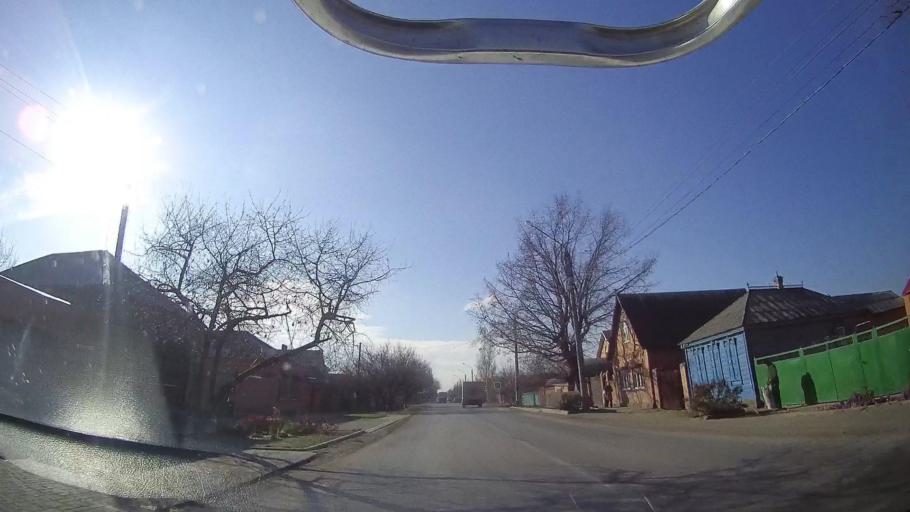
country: RU
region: Rostov
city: Bataysk
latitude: 47.1331
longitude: 39.7003
